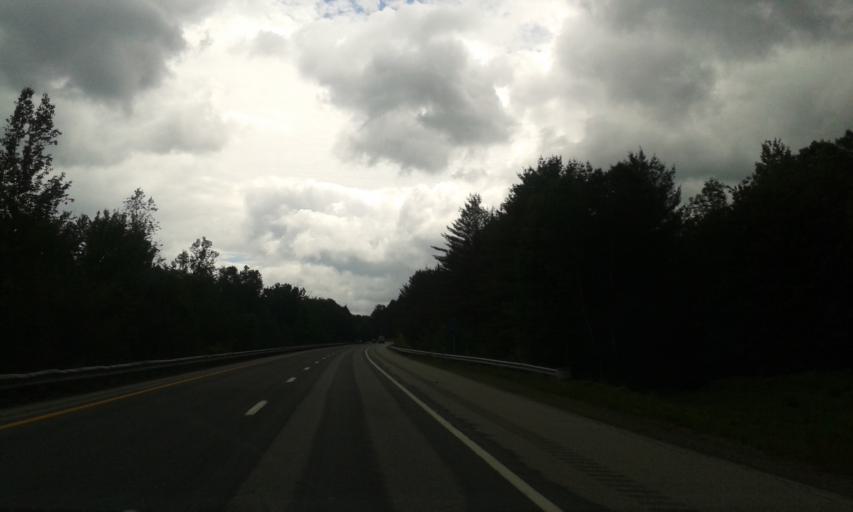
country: US
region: New Hampshire
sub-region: Grafton County
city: Woodstock
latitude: 43.9525
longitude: -71.6840
